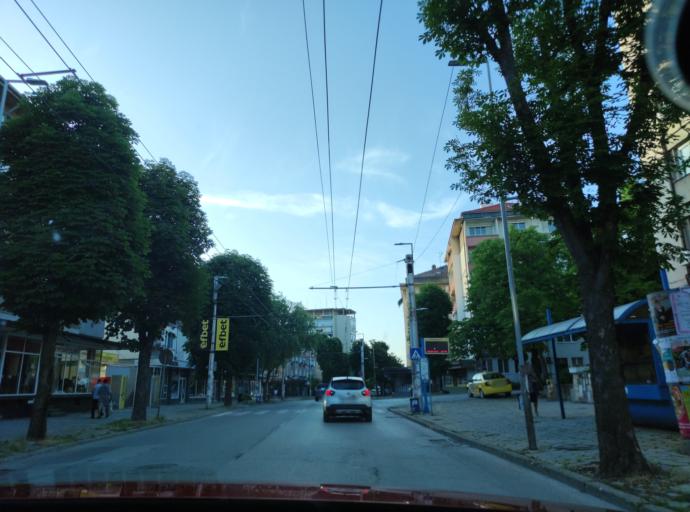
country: BG
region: Pleven
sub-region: Obshtina Pleven
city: Pleven
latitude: 43.4013
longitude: 24.6216
